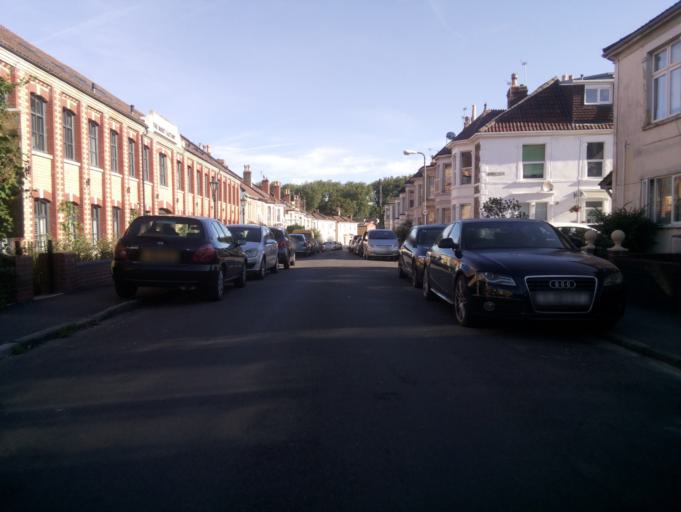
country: GB
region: England
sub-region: South Gloucestershire
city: Kingswood
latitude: 51.4585
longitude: -2.5442
